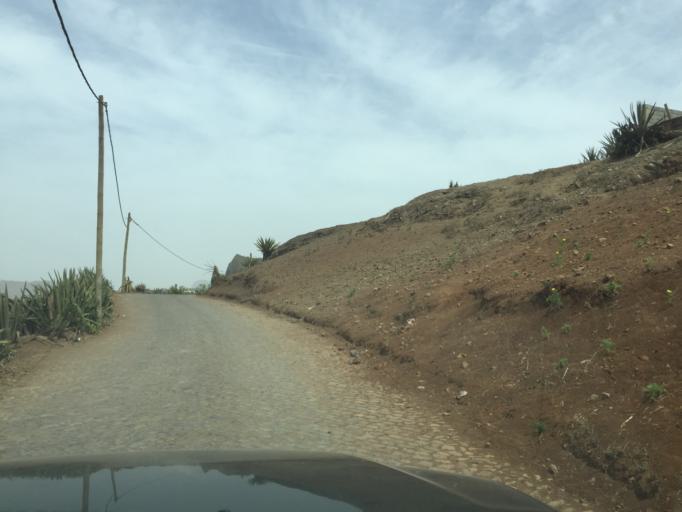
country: CV
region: Santa Catarina
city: Assomada
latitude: 15.1076
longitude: -23.6620
